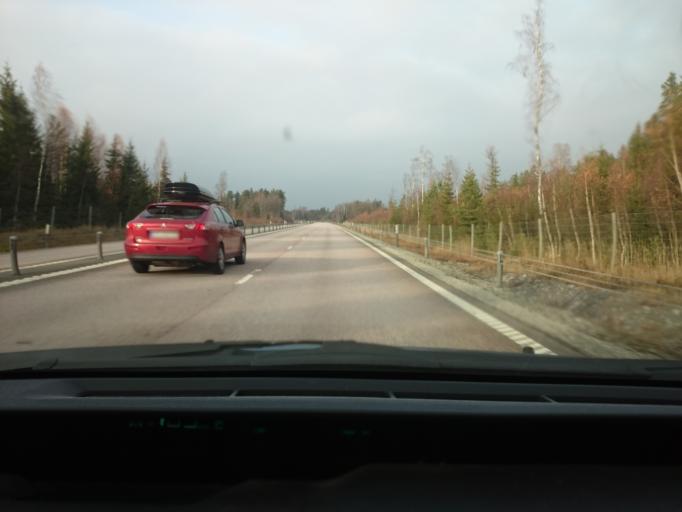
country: SE
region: Vaestmanland
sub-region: Sala Kommun
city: Sala
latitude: 59.9432
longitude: 16.5075
